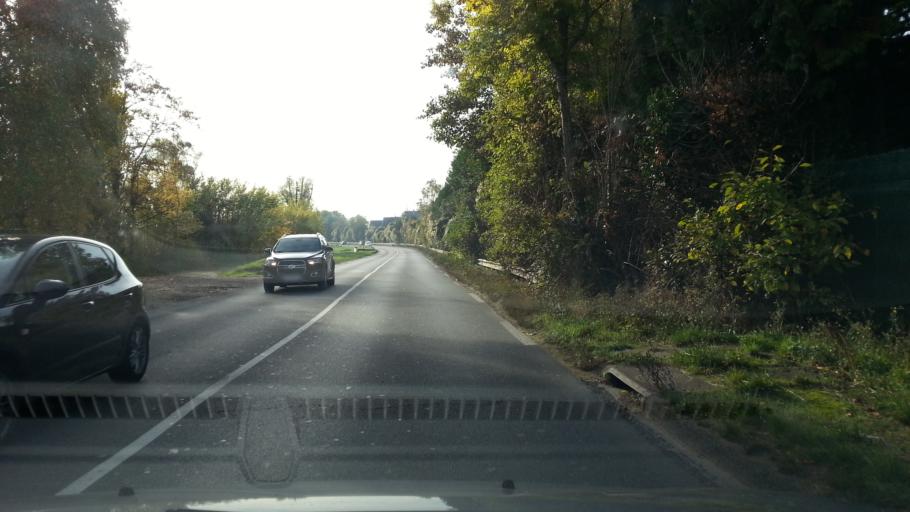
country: FR
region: Picardie
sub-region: Departement de l'Oise
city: Villers-sous-Saint-Leu
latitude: 49.2145
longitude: 2.4124
